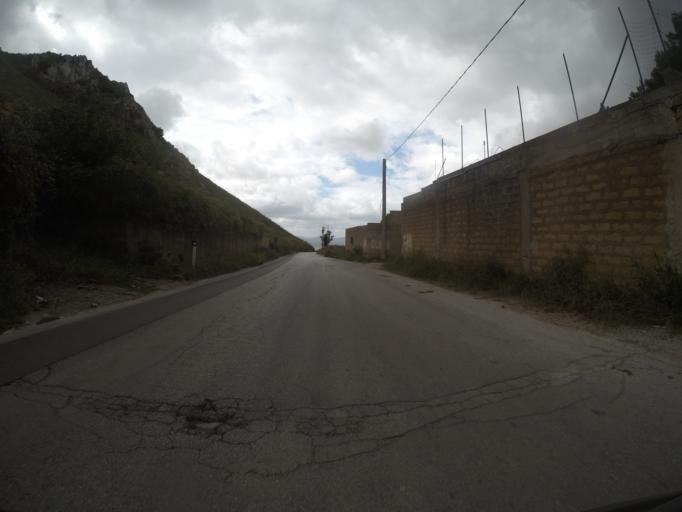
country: IT
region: Sicily
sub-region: Palermo
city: Montelepre
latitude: 38.0996
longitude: 13.1690
